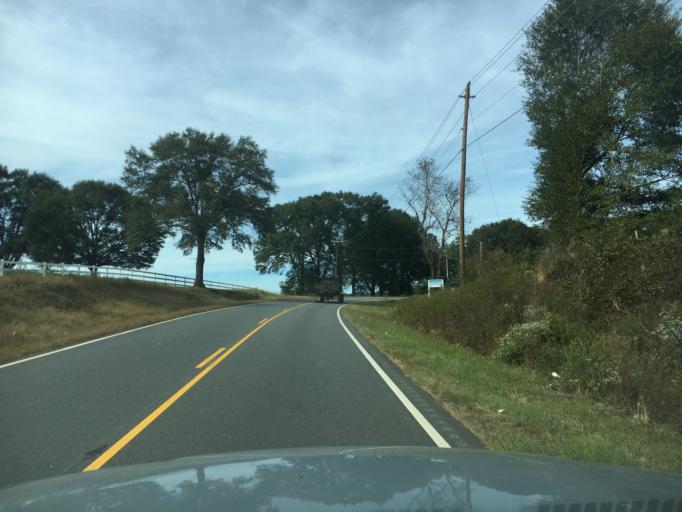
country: US
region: South Carolina
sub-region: Spartanburg County
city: Duncan
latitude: 34.9273
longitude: -82.1457
